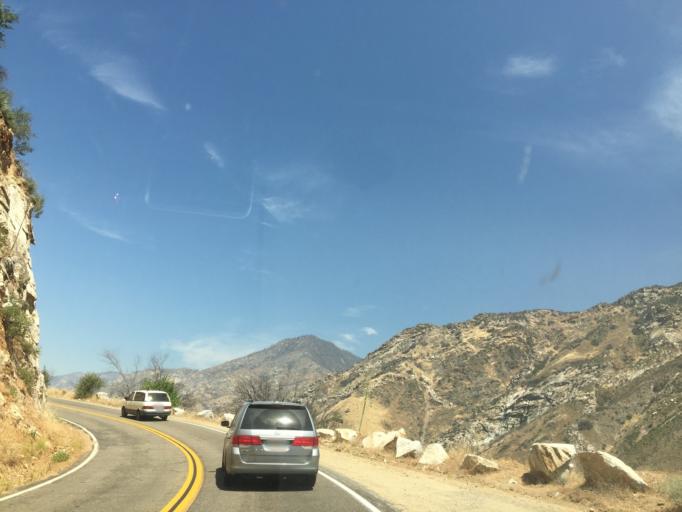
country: US
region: California
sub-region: Tulare County
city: Three Rivers
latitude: 36.8259
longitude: -118.8530
